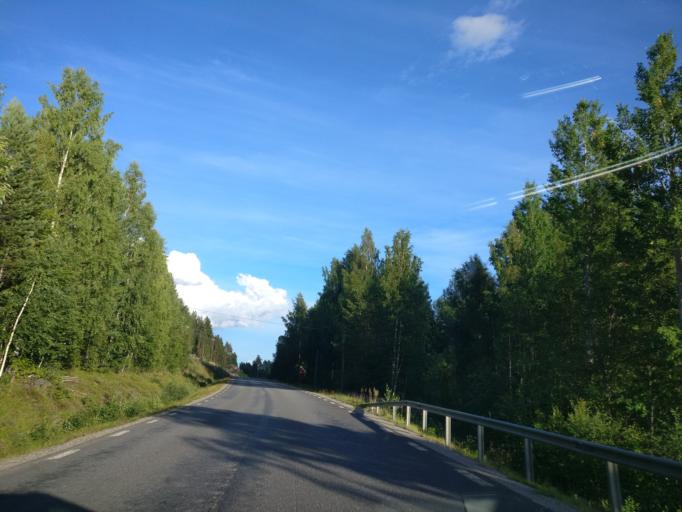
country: SE
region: Jaemtland
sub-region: Braecke Kommun
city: Braecke
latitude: 62.3931
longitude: 15.0391
